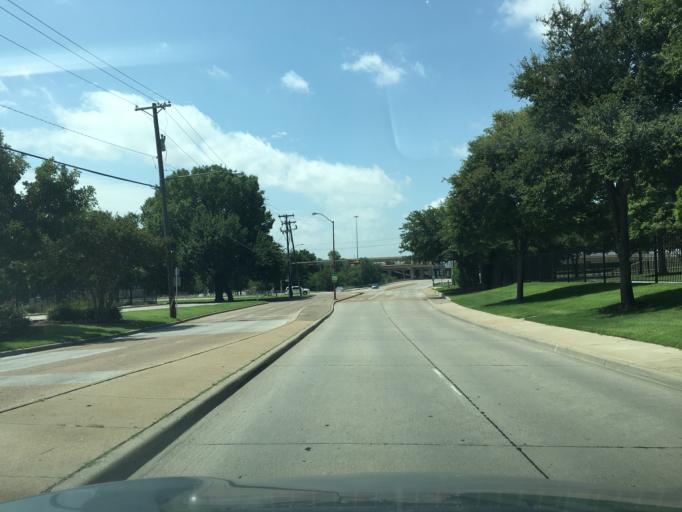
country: US
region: Texas
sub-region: Dallas County
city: Richardson
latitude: 32.9243
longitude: -96.7496
